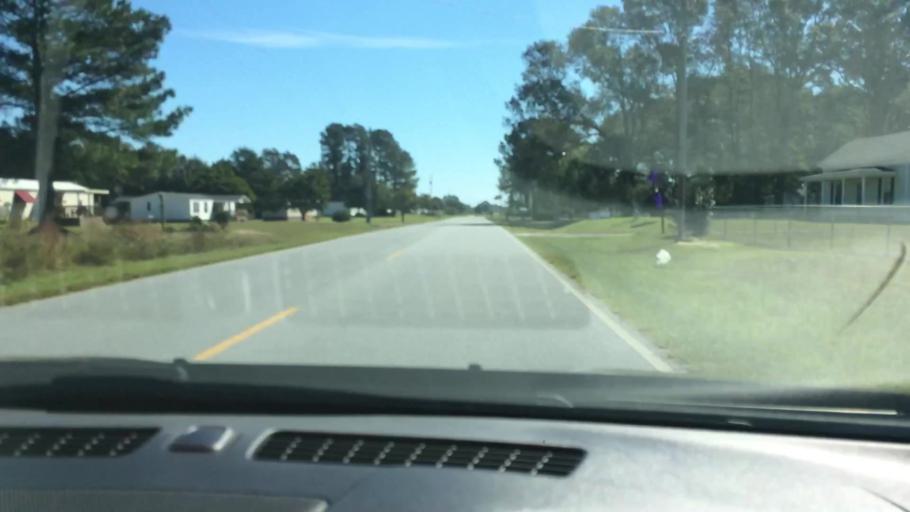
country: US
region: North Carolina
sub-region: Pitt County
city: Grifton
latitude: 35.3885
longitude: -77.3840
